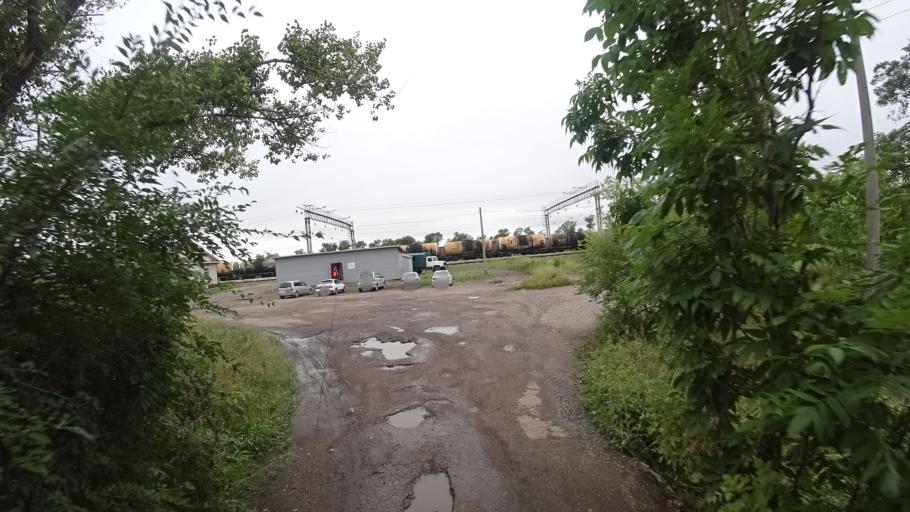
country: RU
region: Primorskiy
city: Chernigovka
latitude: 44.3396
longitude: 132.5341
